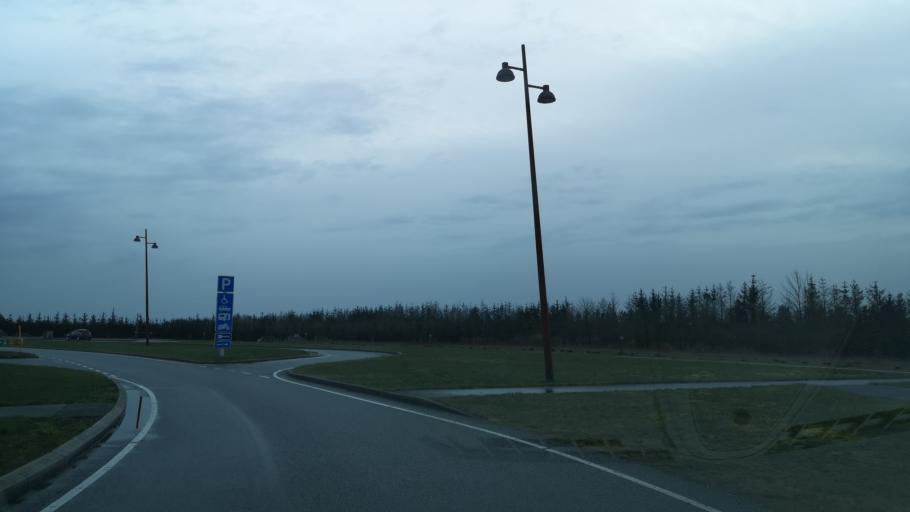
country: DK
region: Central Jutland
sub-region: Herning Kommune
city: Lind
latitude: 56.0392
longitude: 8.9999
